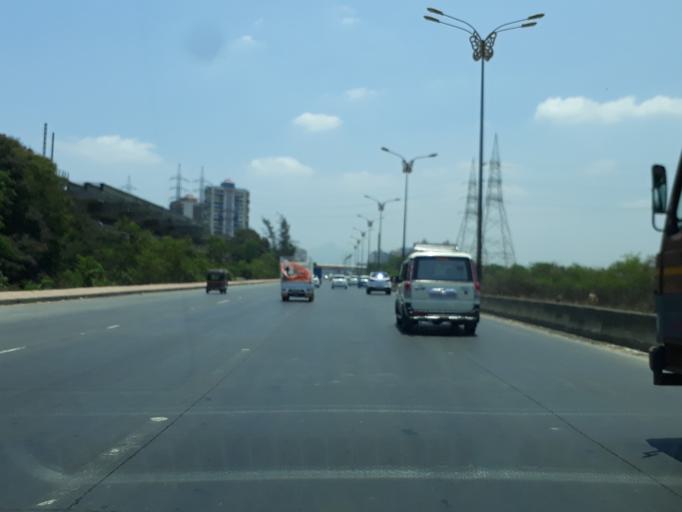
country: IN
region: Maharashtra
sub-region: Thane
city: Artist Village
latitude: 19.0239
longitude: 73.0537
